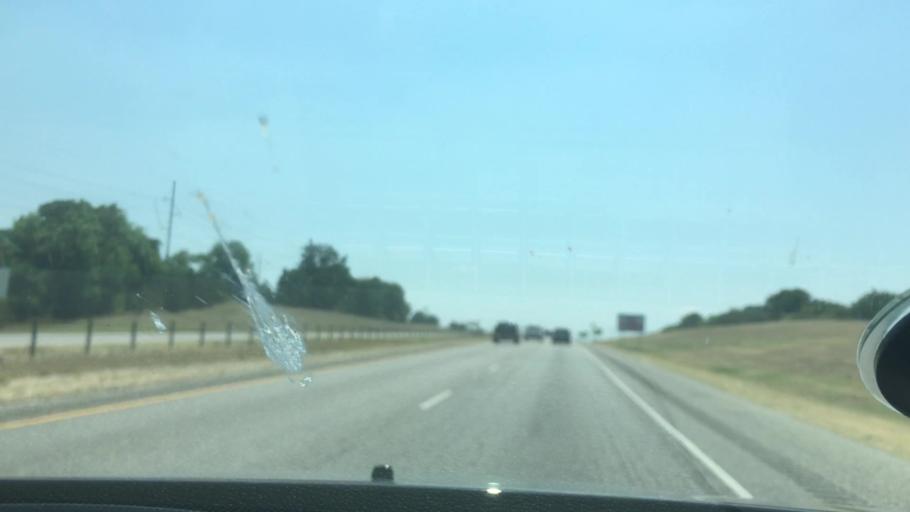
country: US
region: Oklahoma
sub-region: Bryan County
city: Durant
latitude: 34.0139
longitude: -96.3941
